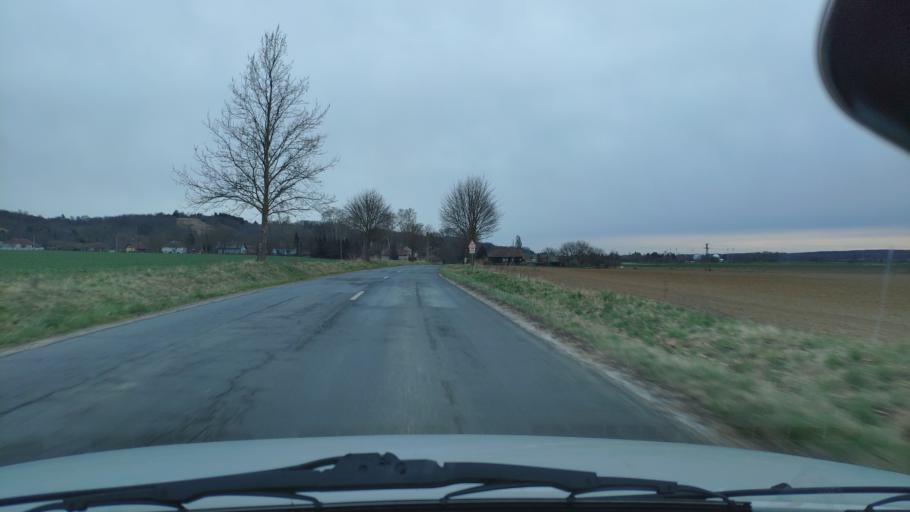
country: HU
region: Zala
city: Nagykanizsa
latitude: 46.5580
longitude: 16.9897
